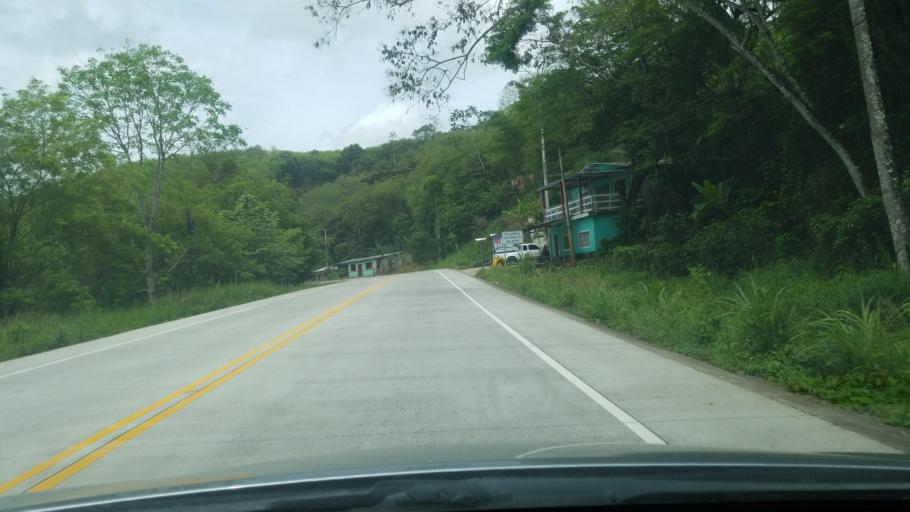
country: HN
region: Copan
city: Trinidad de Copan
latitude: 14.9407
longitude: -88.7650
